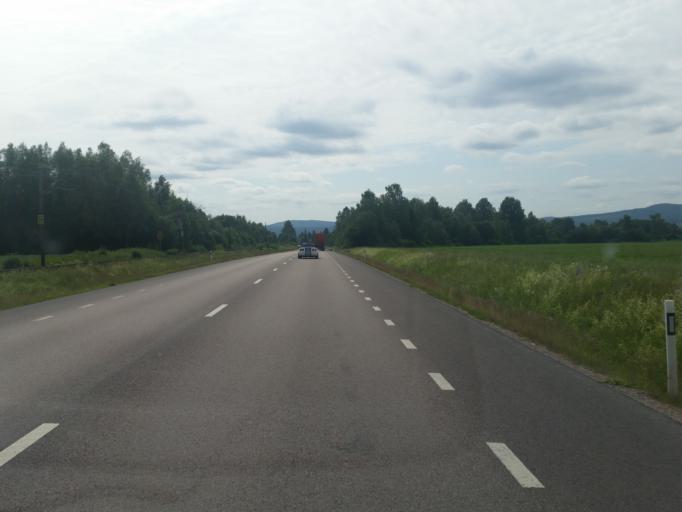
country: SE
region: Dalarna
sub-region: Gagnefs Kommun
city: Djuras
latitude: 60.5716
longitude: 15.1247
